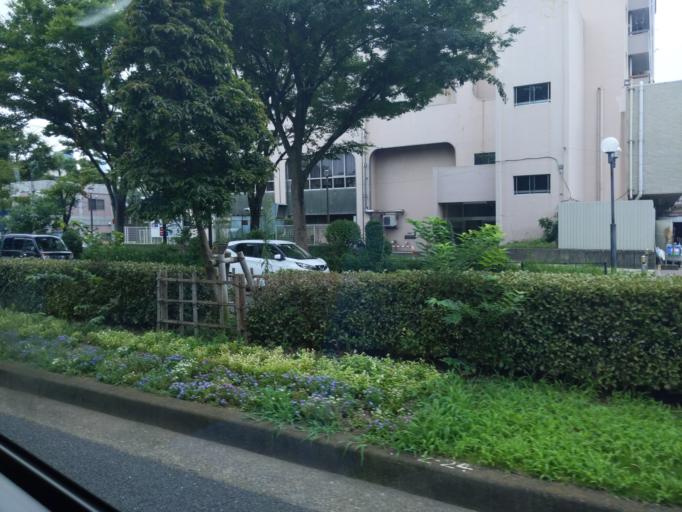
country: JP
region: Saitama
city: Shimotoda
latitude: 35.7881
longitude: 139.6597
